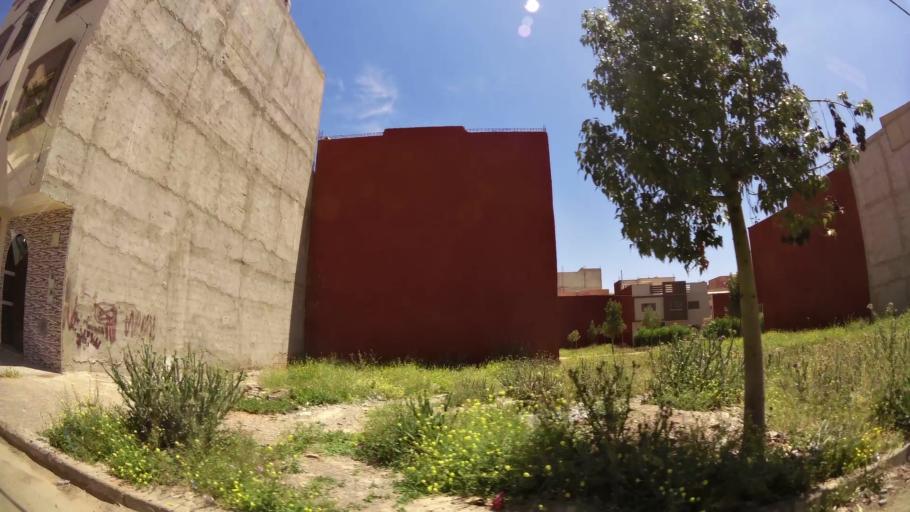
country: MA
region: Oriental
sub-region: Oujda-Angad
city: Oujda
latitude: 34.6656
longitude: -1.9403
